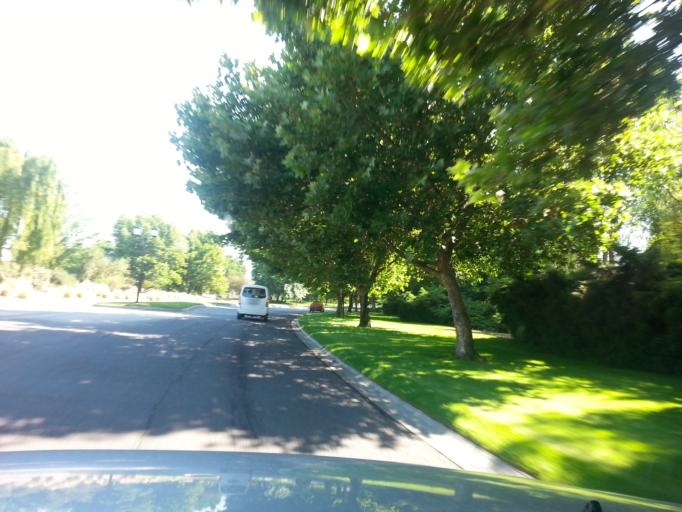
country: CL
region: Santiago Metropolitan
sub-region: Provincia de Chacabuco
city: Chicureo Abajo
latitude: -33.2385
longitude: -70.6745
